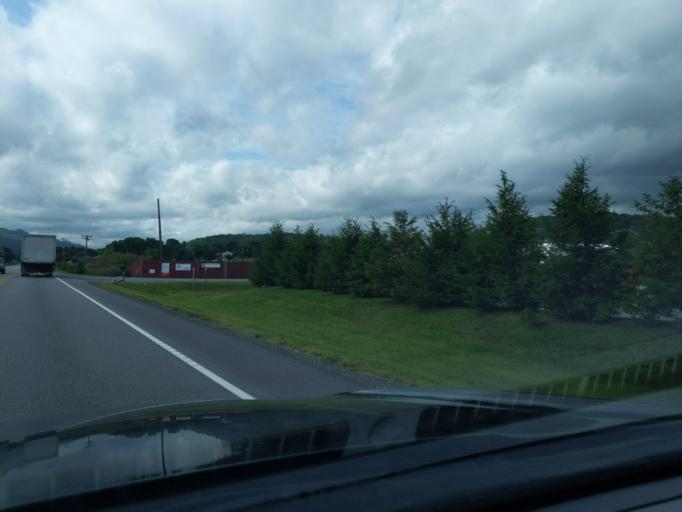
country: US
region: Pennsylvania
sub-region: Blair County
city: Roaring Spring
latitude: 40.3643
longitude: -78.4299
